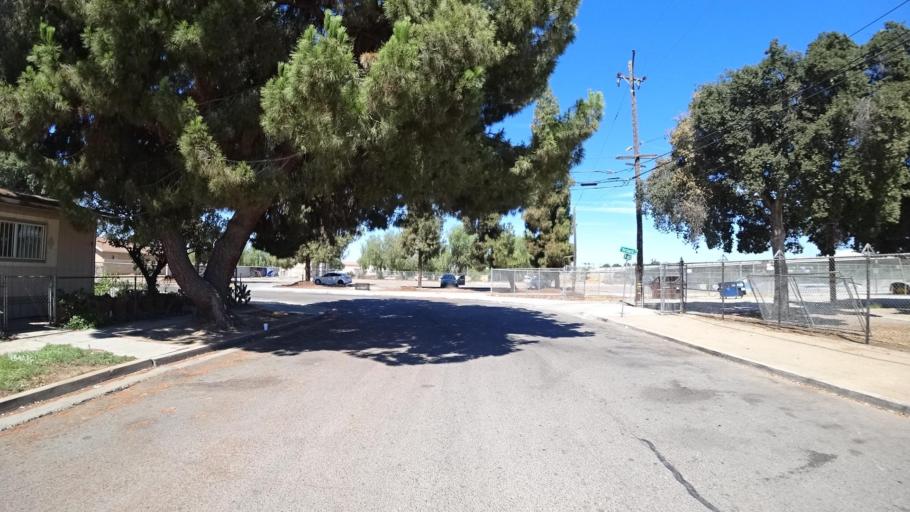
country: US
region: California
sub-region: Fresno County
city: Fresno
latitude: 36.7523
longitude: -119.7746
